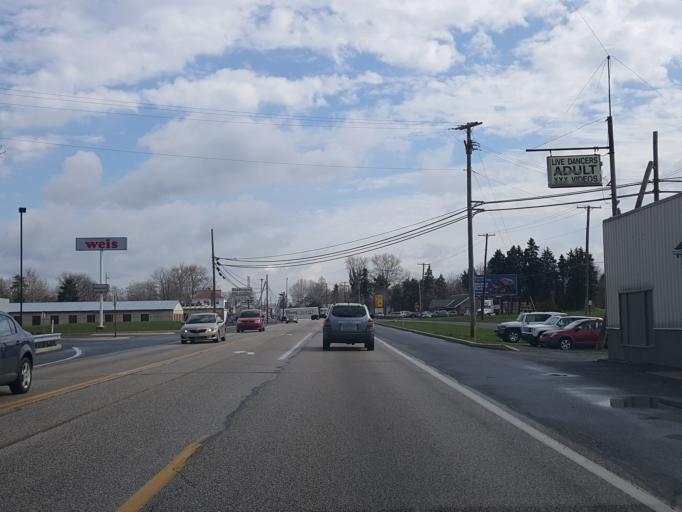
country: US
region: Pennsylvania
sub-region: Lebanon County
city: Avon
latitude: 40.3499
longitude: -76.3824
